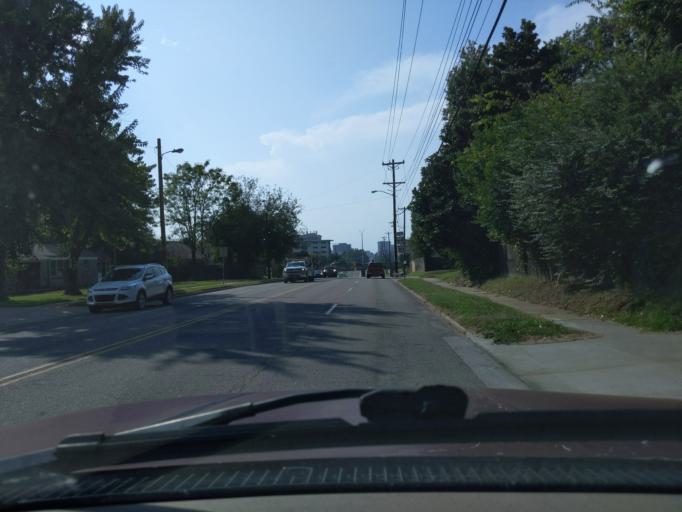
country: US
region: Oklahoma
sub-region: Tulsa County
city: Tulsa
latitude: 36.1333
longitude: -95.9464
